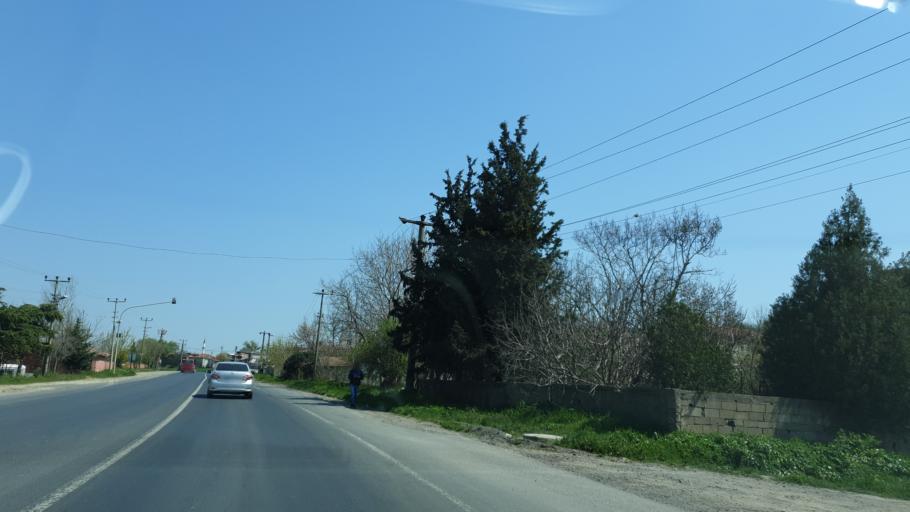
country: TR
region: Tekirdag
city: Corlu
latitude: 41.1681
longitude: 27.7917
